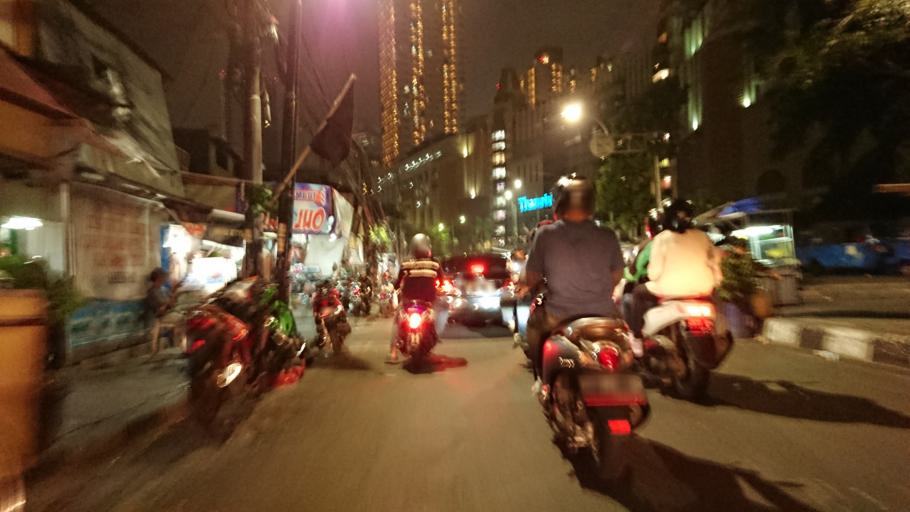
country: ID
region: Jakarta Raya
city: Jakarta
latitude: -6.1931
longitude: 106.8150
